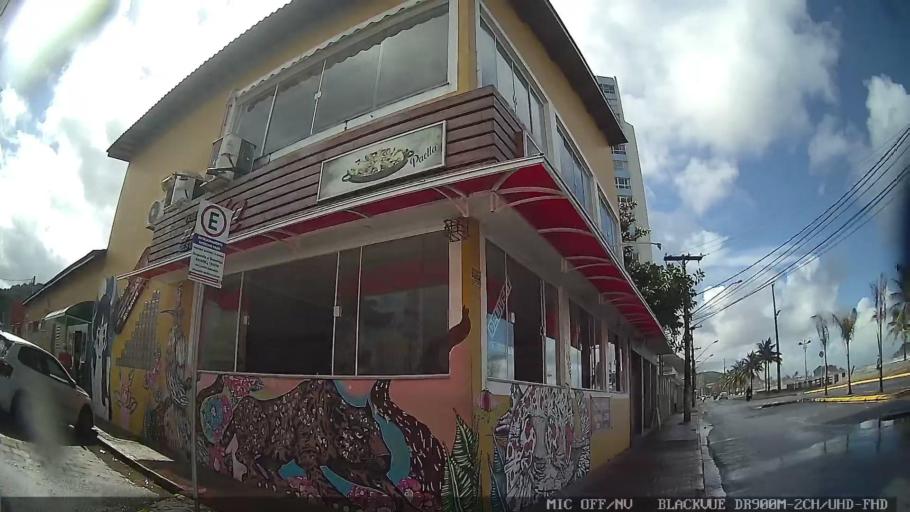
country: BR
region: Sao Paulo
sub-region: Itanhaem
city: Itanhaem
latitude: -24.1878
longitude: -46.8016
